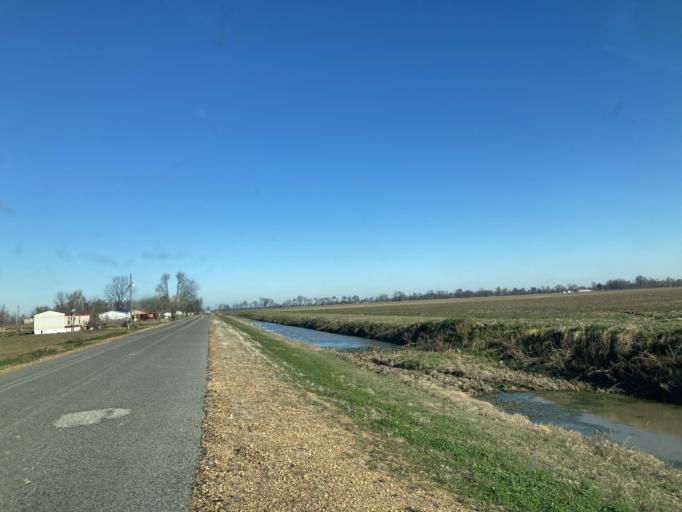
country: US
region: Mississippi
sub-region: Yazoo County
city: Yazoo City
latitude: 32.9534
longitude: -90.6055
